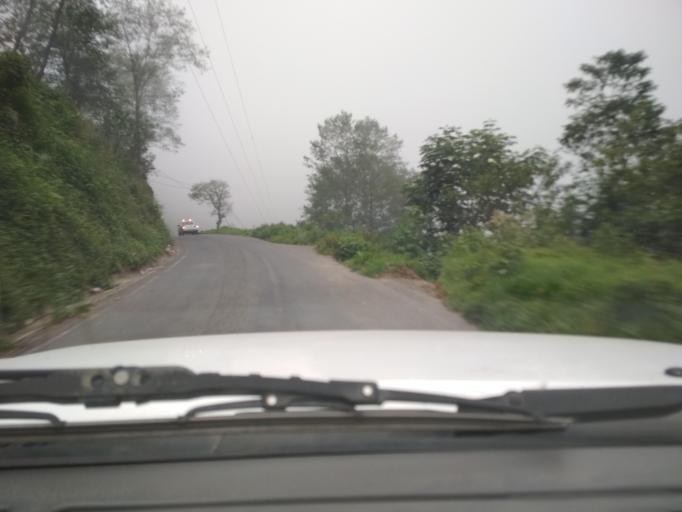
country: MX
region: Veracruz
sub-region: La Perla
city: Metlac Hernandez (Metlac Primero)
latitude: 18.9693
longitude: -97.1467
